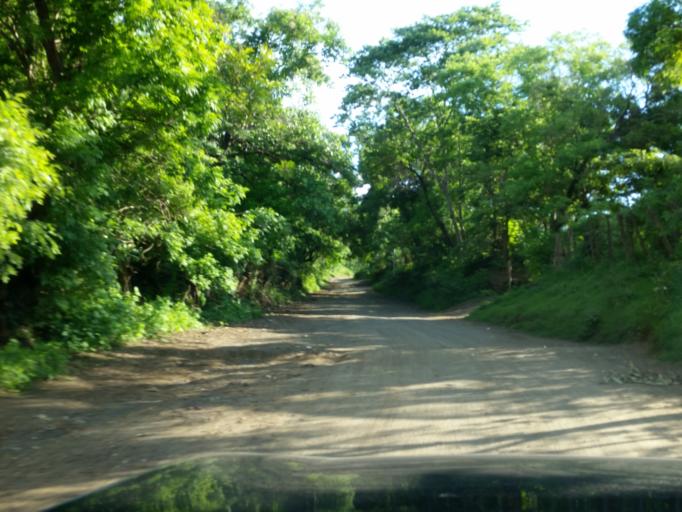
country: NI
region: Managua
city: Managua
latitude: 12.0914
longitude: -86.2036
